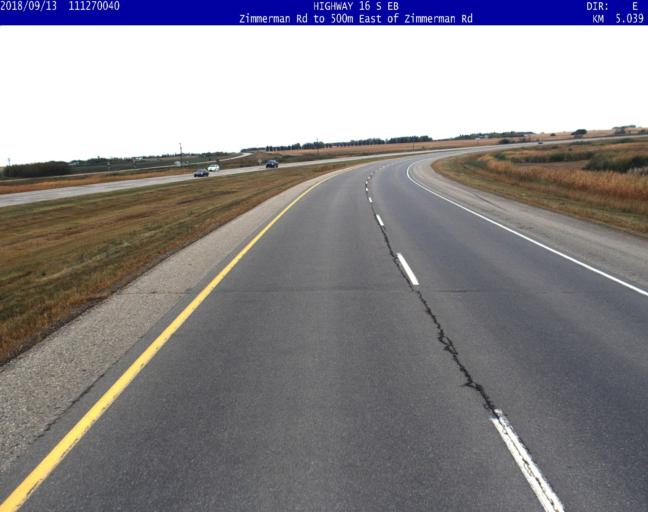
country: CA
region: Saskatchewan
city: Saskatoon
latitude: 52.0858
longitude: -106.5250
